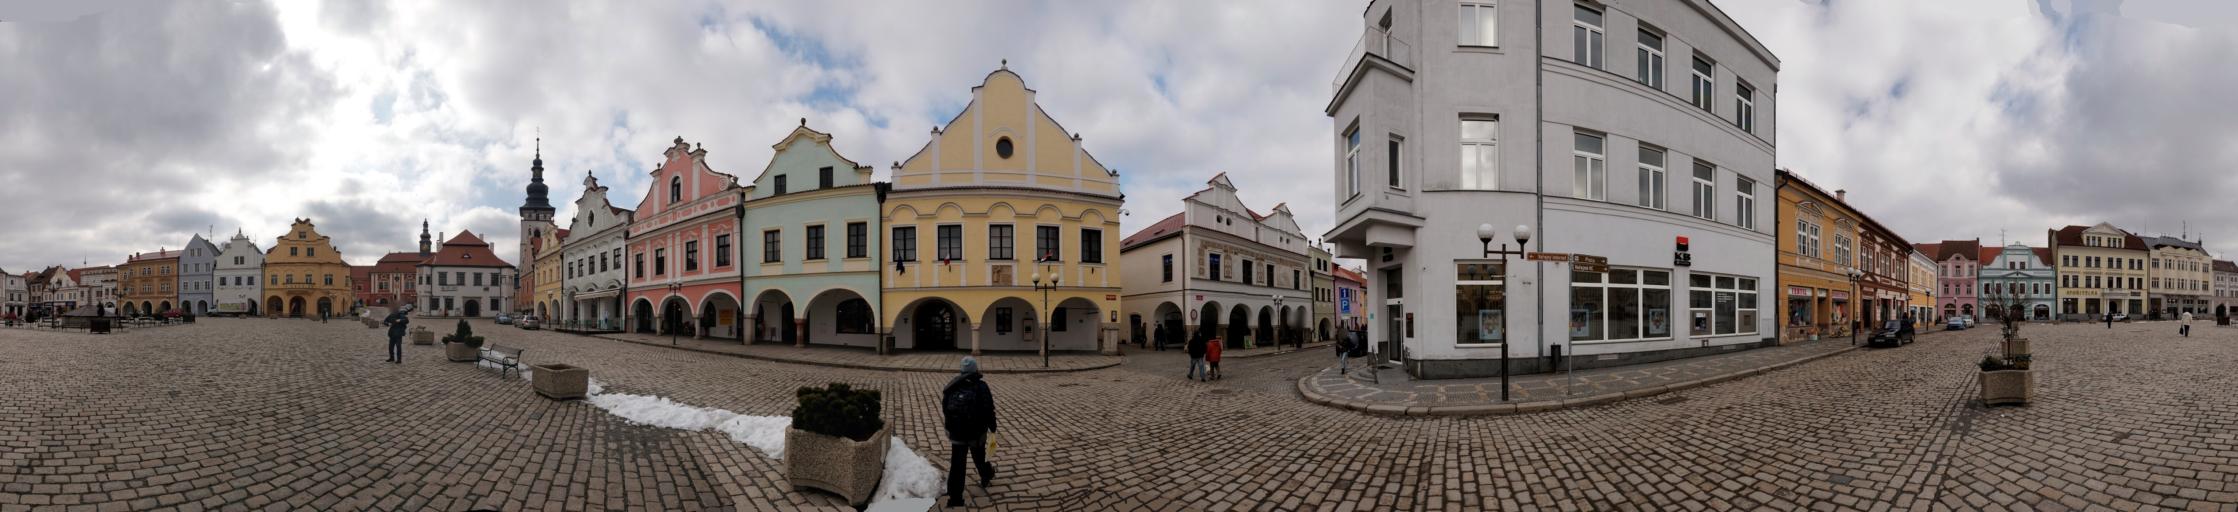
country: CZ
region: Vysocina
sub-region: Okres Pelhrimov
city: Pelhrimov
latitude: 49.4312
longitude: 15.2234
